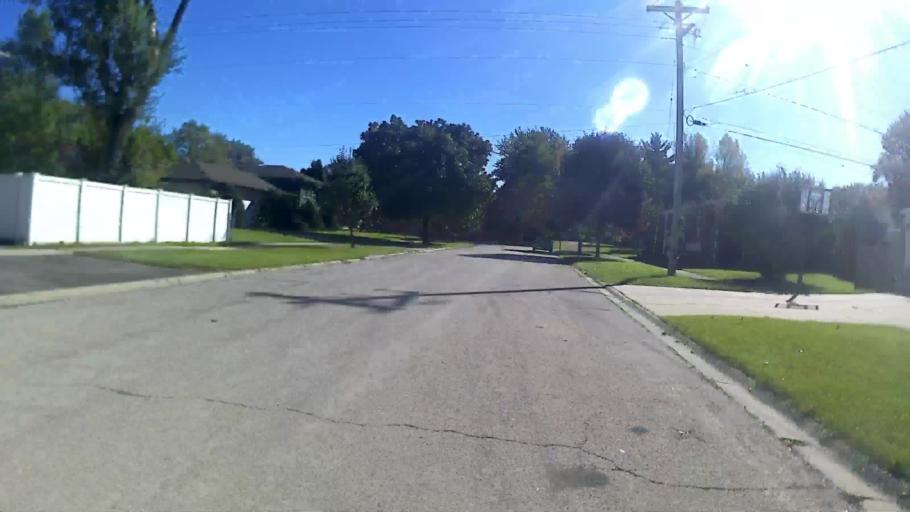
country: US
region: Illinois
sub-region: DuPage County
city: Wood Dale
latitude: 41.9551
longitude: -87.9959
